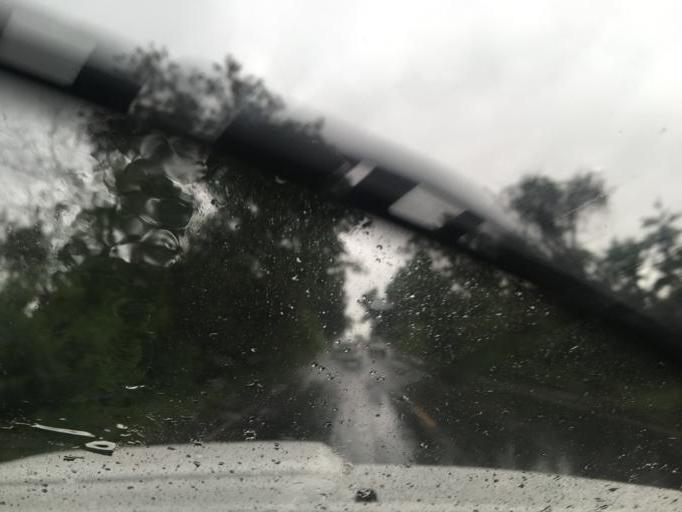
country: TH
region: Changwat Udon Thani
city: Udon Thani
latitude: 17.3107
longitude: 102.7093
